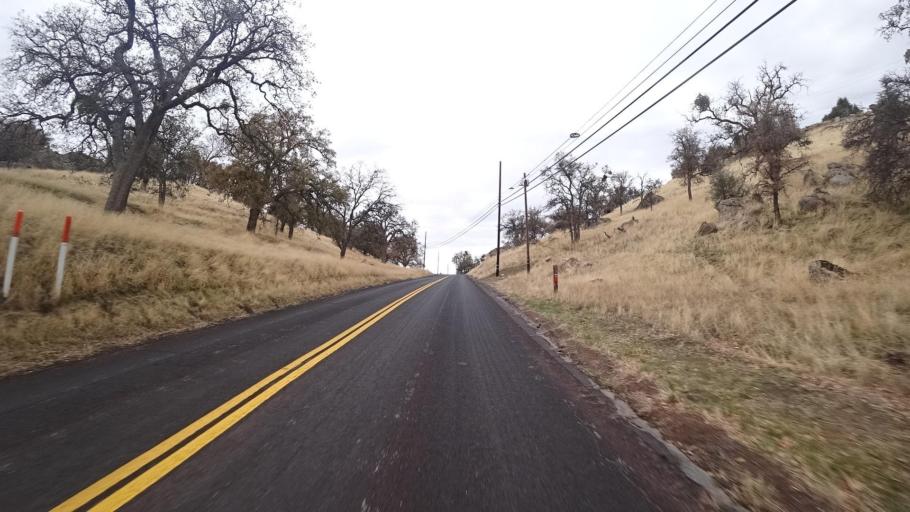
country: US
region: California
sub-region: Kern County
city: Stallion Springs
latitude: 35.0926
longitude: -118.6540
